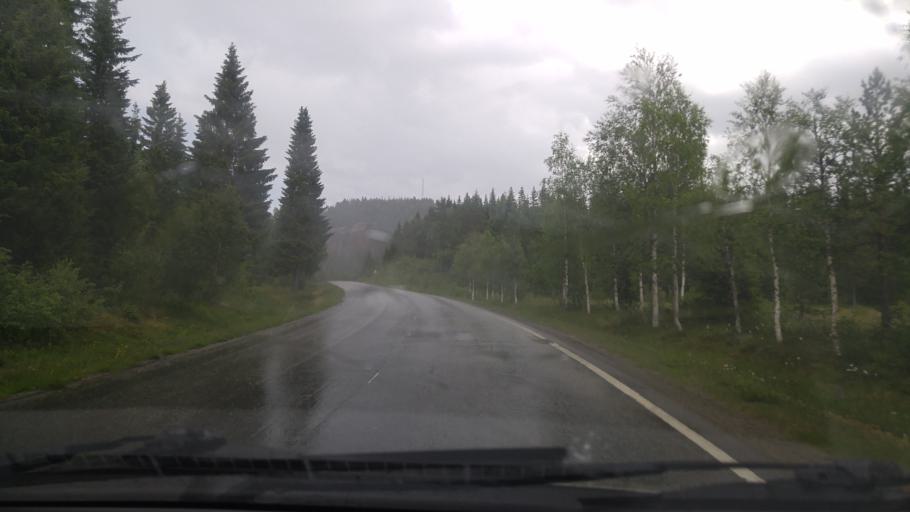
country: NO
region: Nord-Trondelag
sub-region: Namdalseid
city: Namdalseid
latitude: 64.3401
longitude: 11.2839
